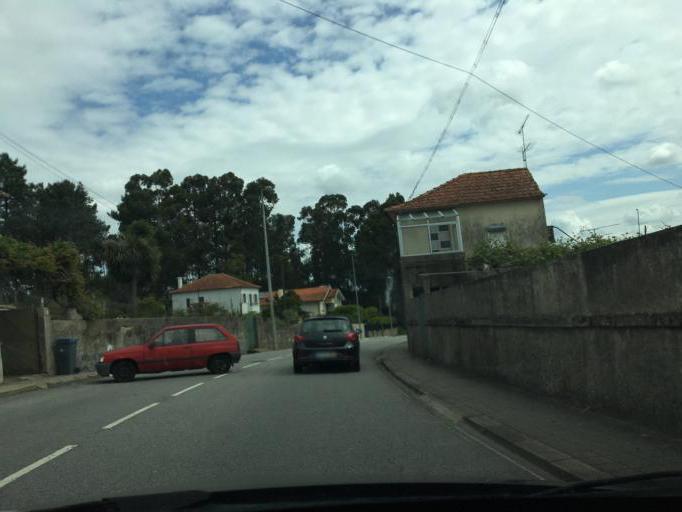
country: PT
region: Porto
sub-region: Maia
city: Maia
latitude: 41.2428
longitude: -8.6209
